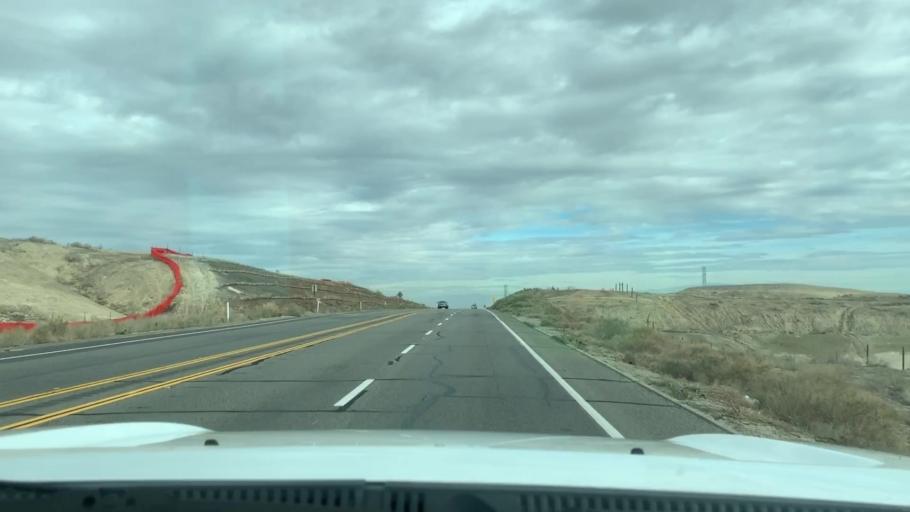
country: US
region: California
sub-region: Kern County
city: Ford City
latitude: 35.2553
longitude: -119.3306
